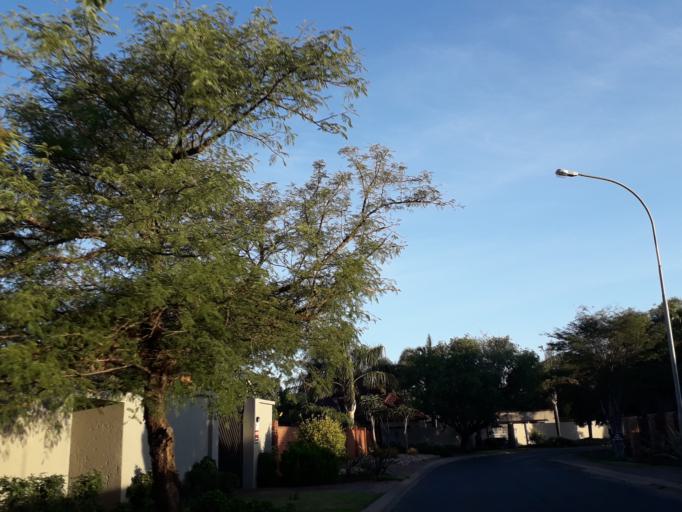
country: ZA
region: Gauteng
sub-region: City of Johannesburg Metropolitan Municipality
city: Roodepoort
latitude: -26.1585
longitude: 27.9523
